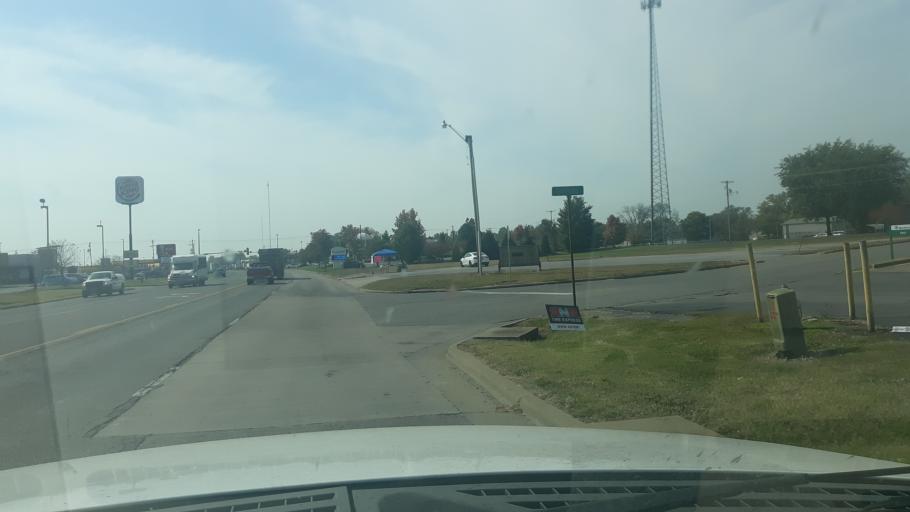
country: US
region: Illinois
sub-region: Saline County
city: Harrisburg
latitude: 37.7334
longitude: -88.5342
